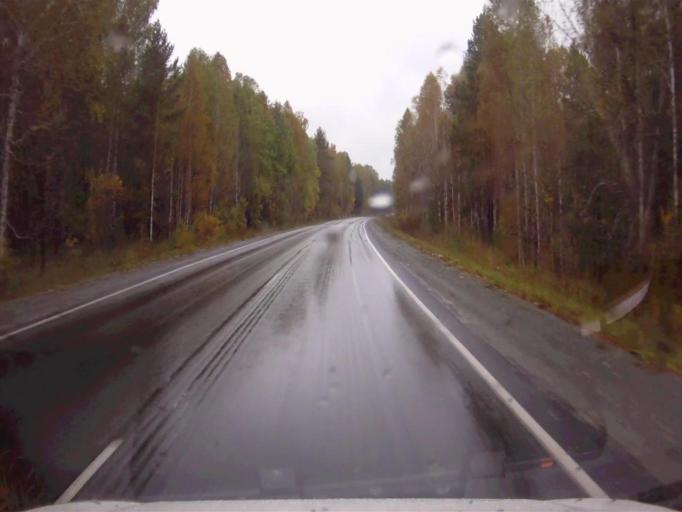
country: RU
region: Chelyabinsk
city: Tayginka
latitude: 55.5973
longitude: 60.6175
